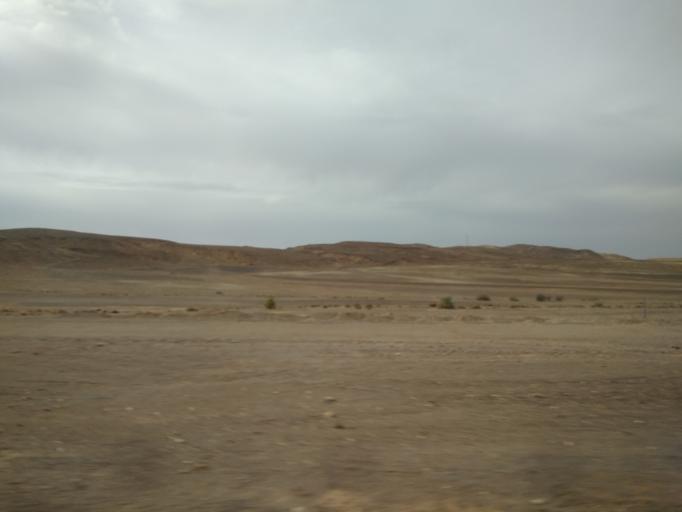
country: IL
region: Southern District
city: Eilat
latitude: 29.9152
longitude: 34.8798
